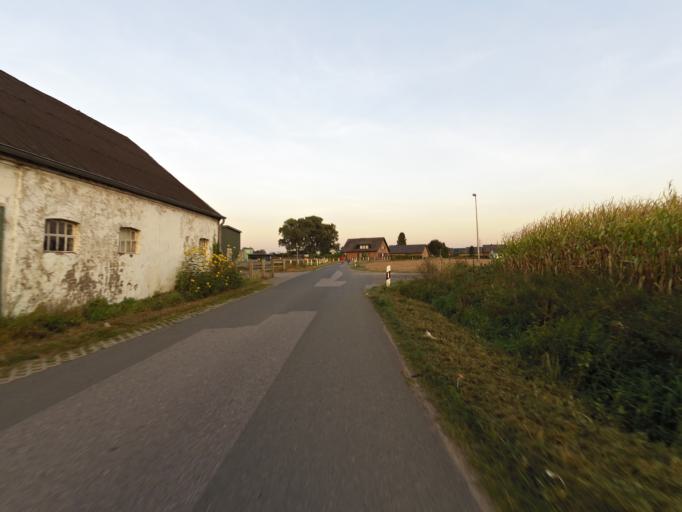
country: DE
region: North Rhine-Westphalia
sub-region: Regierungsbezirk Dusseldorf
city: Emmerich
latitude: 51.8569
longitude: 6.2561
